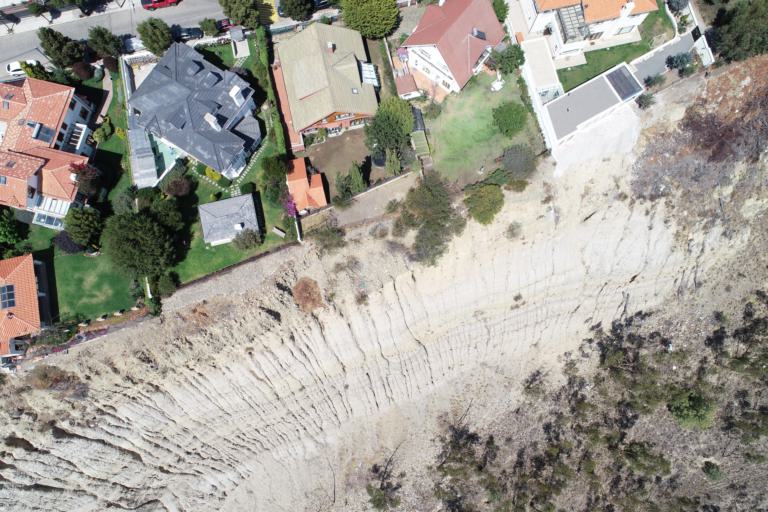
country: BO
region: La Paz
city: La Paz
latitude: -16.5312
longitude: -68.0911
